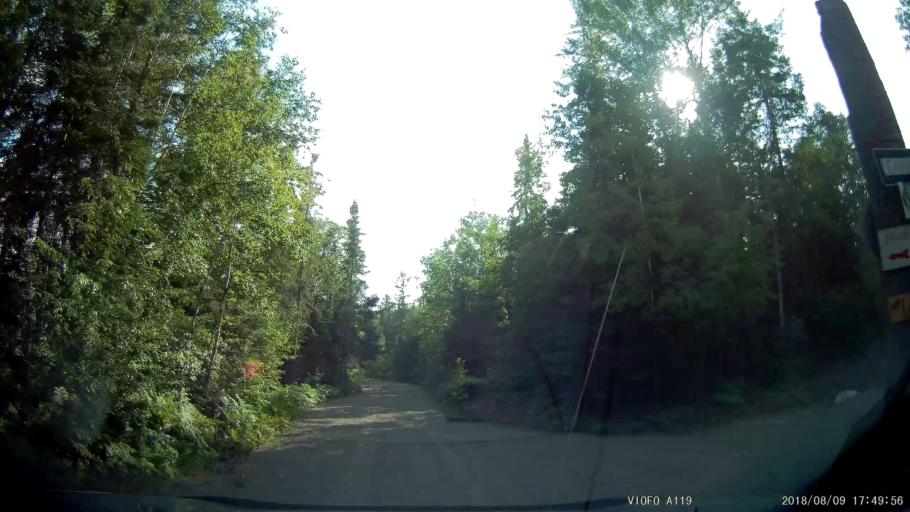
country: CA
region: Ontario
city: Rayside-Balfour
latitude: 46.5877
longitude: -81.5447
